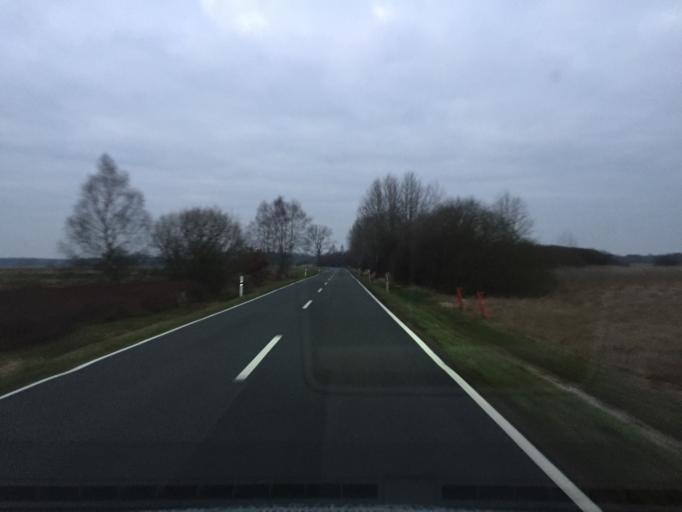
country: DE
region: Lower Saxony
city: Maasen
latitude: 52.6383
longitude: 8.8900
